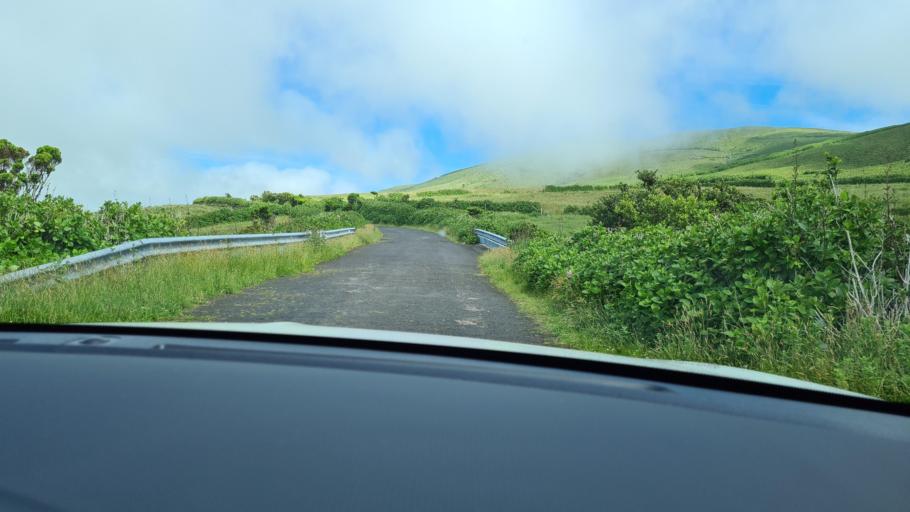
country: PT
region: Azores
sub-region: Sao Roque do Pico
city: Sao Roque do Pico
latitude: 38.6698
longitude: -28.1317
